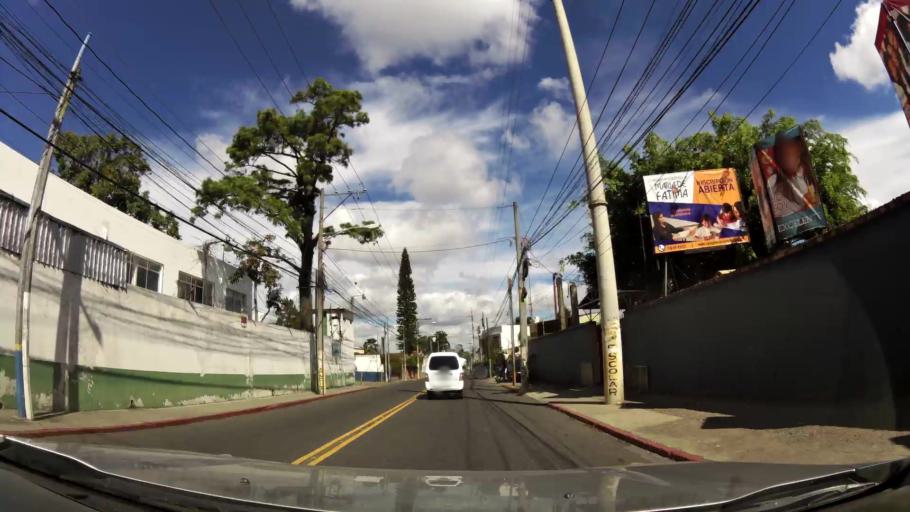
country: GT
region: Guatemala
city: Mixco
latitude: 14.6356
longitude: -90.5661
